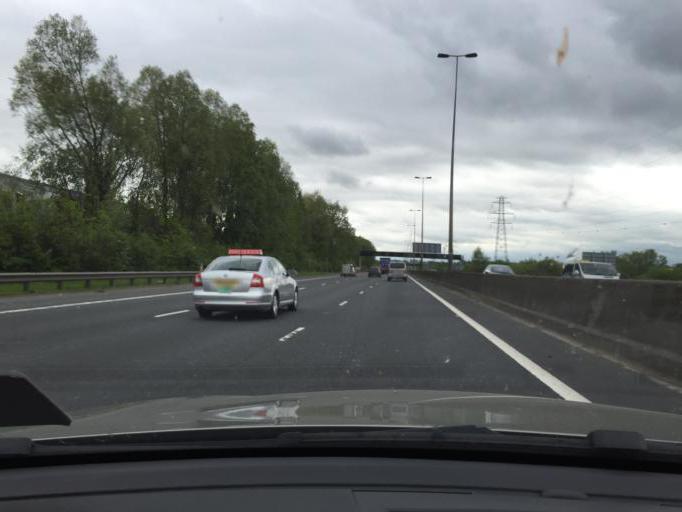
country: GB
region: Northern Ireland
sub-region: City of Belfast
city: Belfast
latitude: 54.5829
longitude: -5.9652
